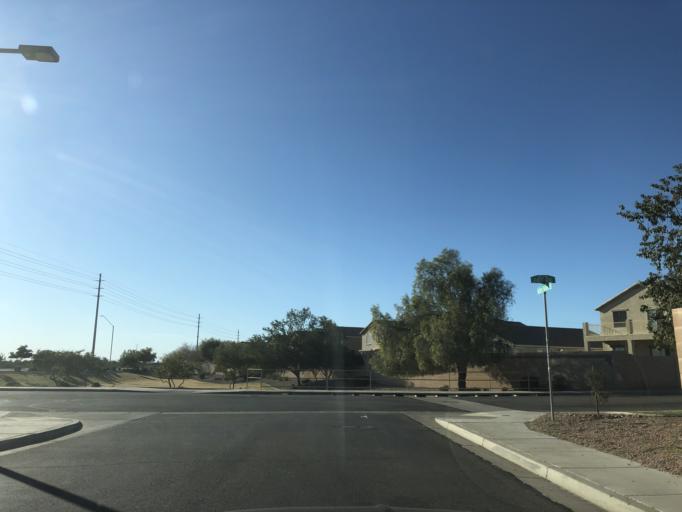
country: US
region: Arizona
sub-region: Maricopa County
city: Buckeye
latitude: 33.4362
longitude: -112.5680
